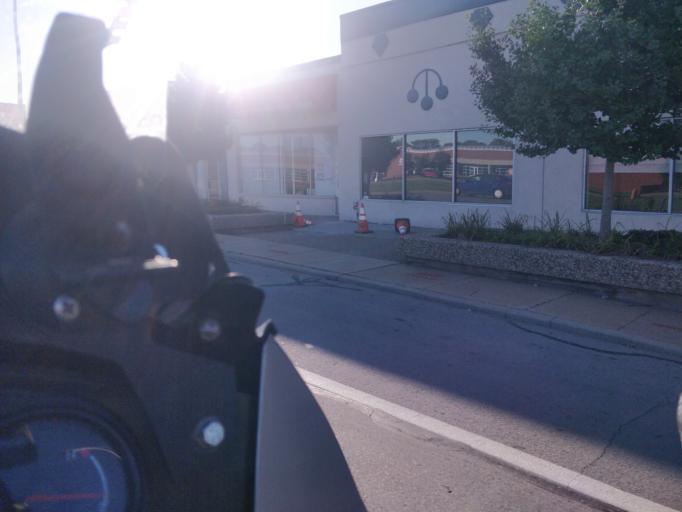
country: US
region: Michigan
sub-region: Wayne County
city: Lincoln Park
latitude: 42.2546
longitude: -83.1736
